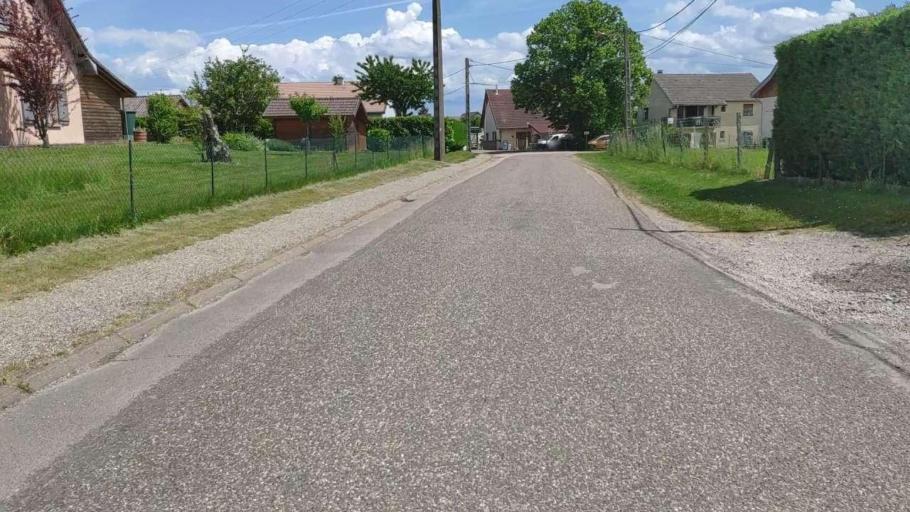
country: FR
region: Franche-Comte
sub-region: Departement du Jura
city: Bletterans
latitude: 46.7621
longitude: 5.4445
